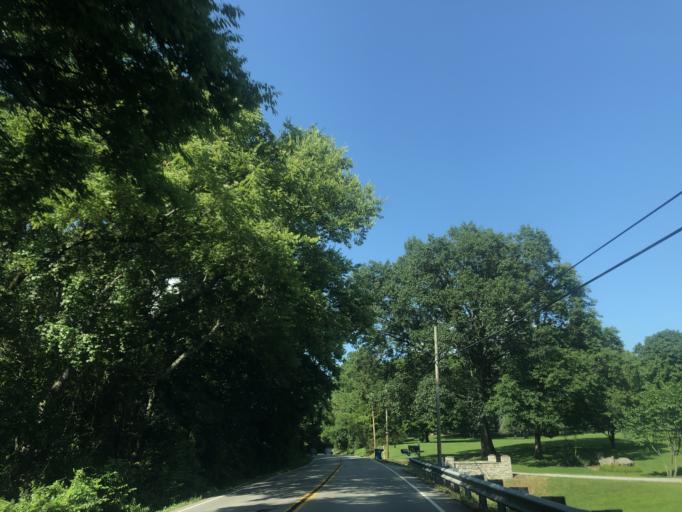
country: US
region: Tennessee
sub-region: Wilson County
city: Green Hill
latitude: 36.1964
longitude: -86.5973
